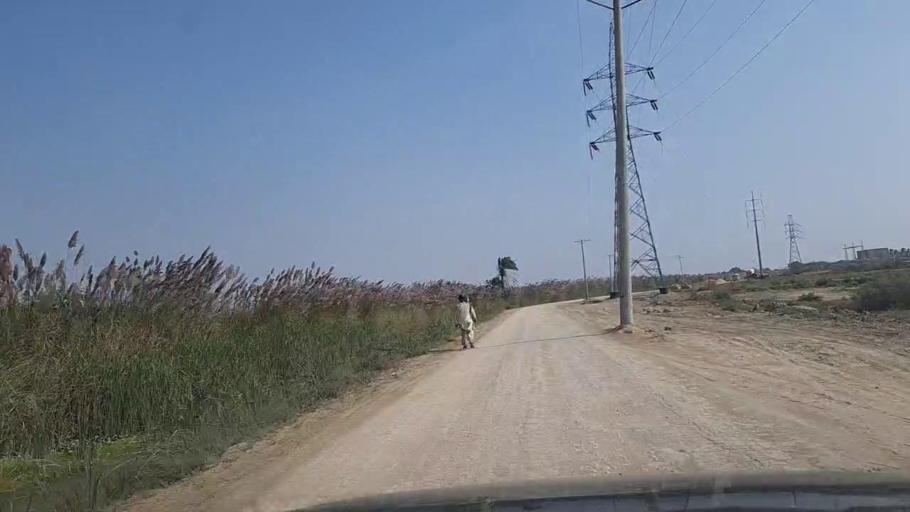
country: PK
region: Sindh
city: Gharo
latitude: 24.7219
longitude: 67.5522
